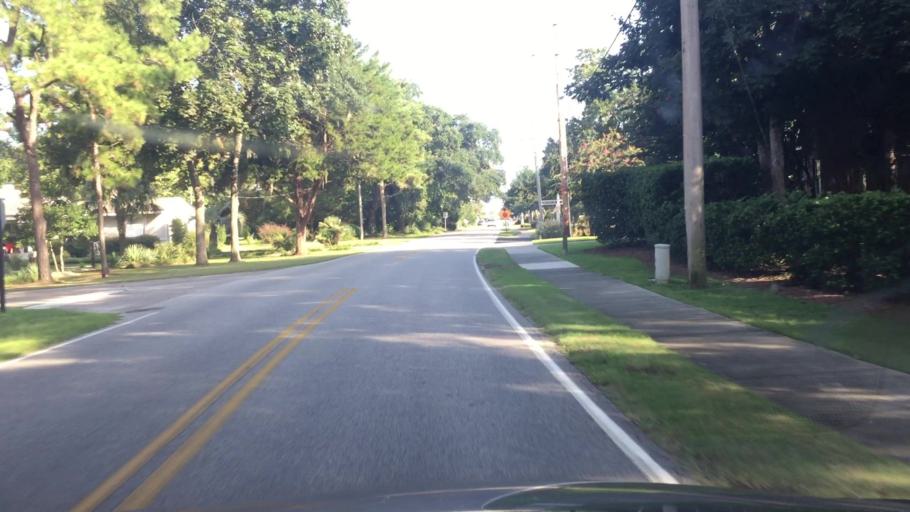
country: US
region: South Carolina
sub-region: Horry County
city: North Myrtle Beach
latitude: 33.8250
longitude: -78.6645
